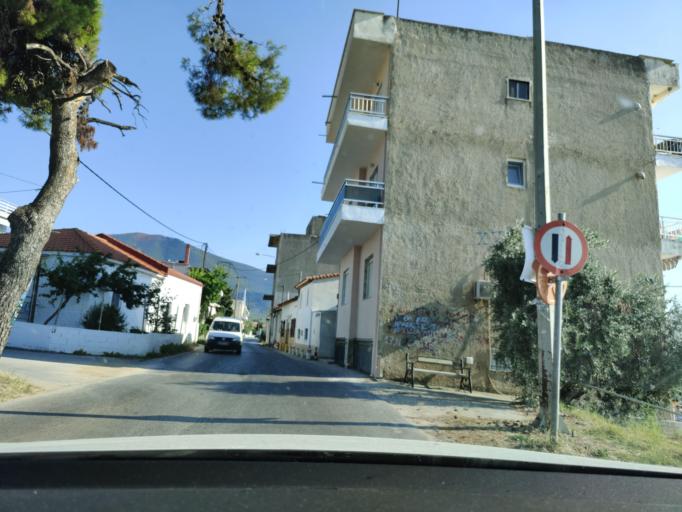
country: GR
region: East Macedonia and Thrace
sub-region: Nomos Kavalas
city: Prinos
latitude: 40.7105
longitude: 24.5340
